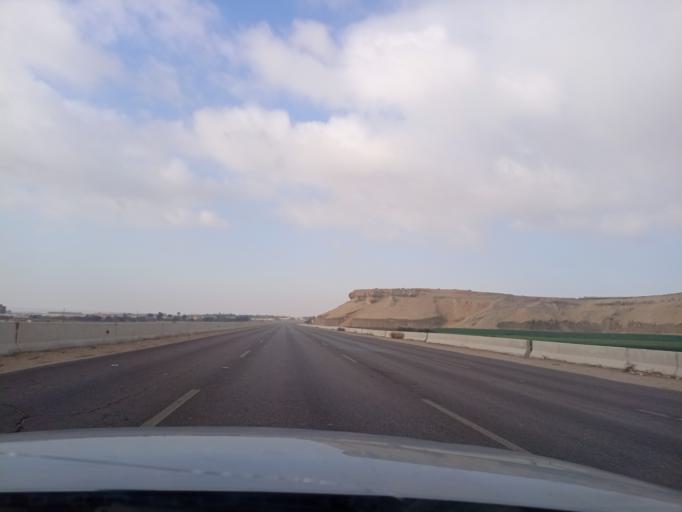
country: EG
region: Al Jizah
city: Al `Ayyat
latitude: 29.6774
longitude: 31.2088
